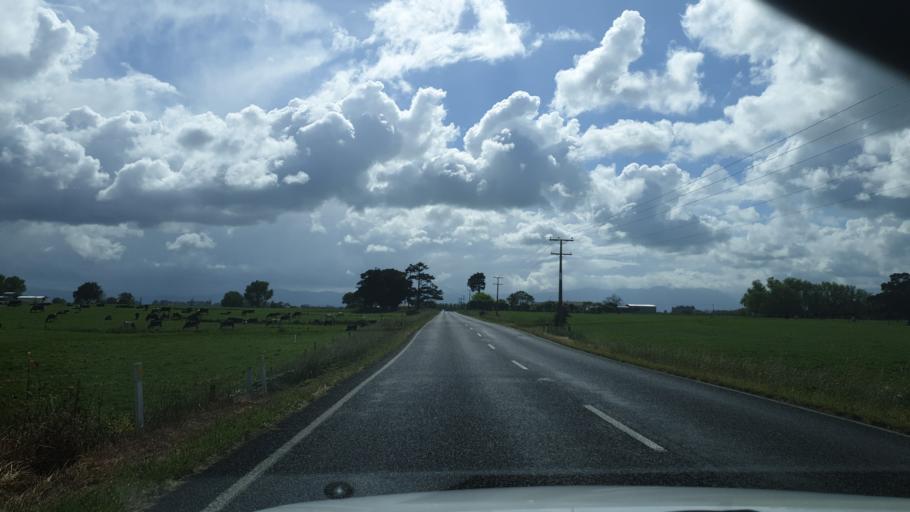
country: NZ
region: Waikato
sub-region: Hauraki District
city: Paeroa
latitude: -37.5138
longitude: 175.5084
